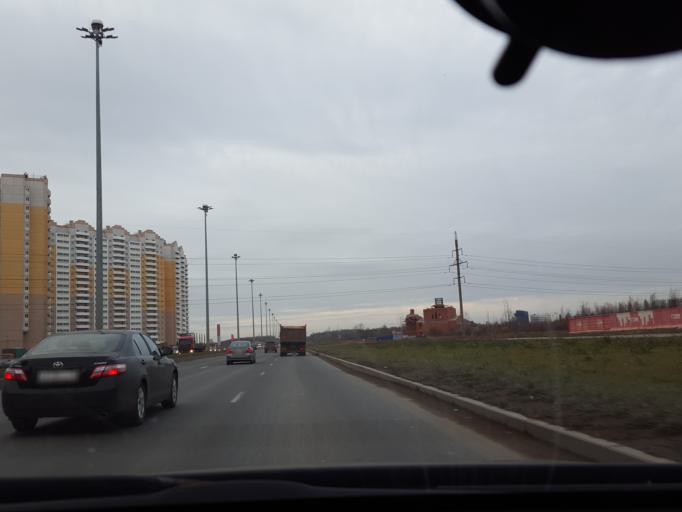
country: RU
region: St.-Petersburg
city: Kolomyagi
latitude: 60.0350
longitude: 30.2480
